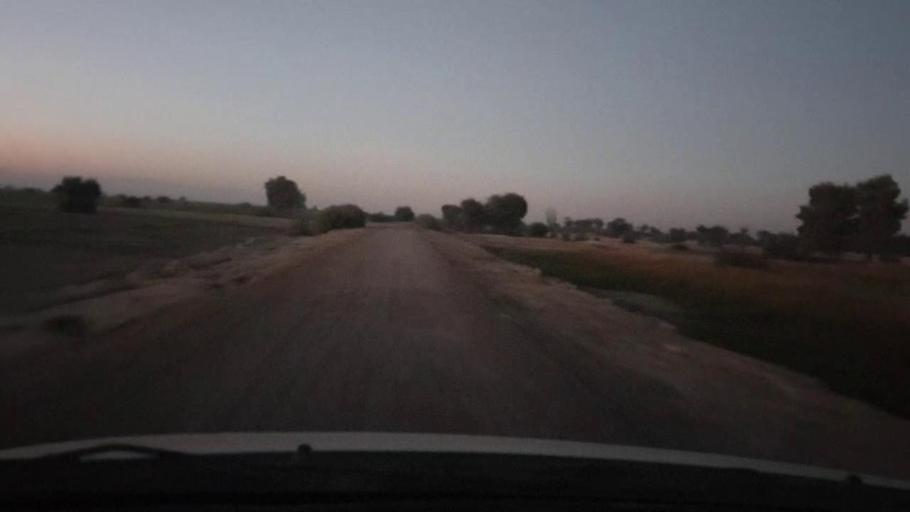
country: PK
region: Sindh
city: Phulji
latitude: 26.9028
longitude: 67.4710
